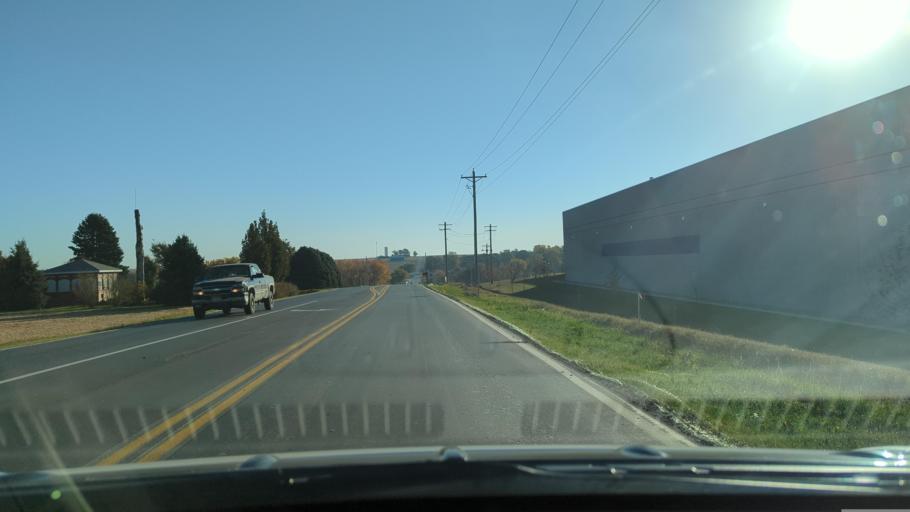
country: US
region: Nebraska
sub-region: Sarpy County
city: Springfield
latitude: 41.0891
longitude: -96.1433
